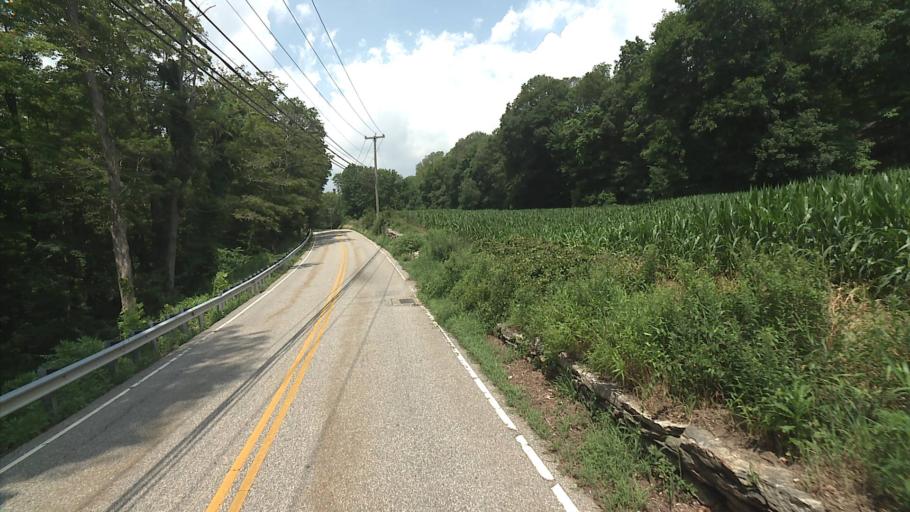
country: US
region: Connecticut
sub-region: New London County
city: Baltic
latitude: 41.6165
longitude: -72.0766
